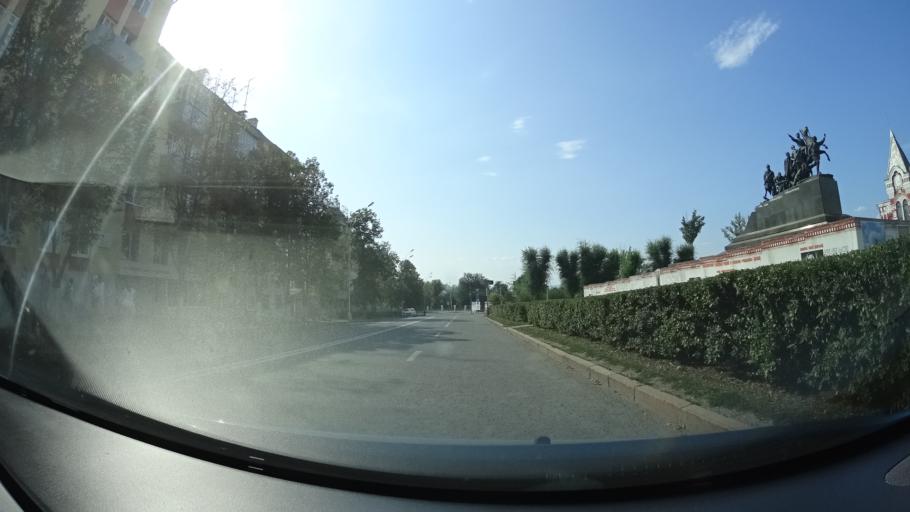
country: RU
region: Samara
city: Samara
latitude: 53.1966
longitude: 50.0973
